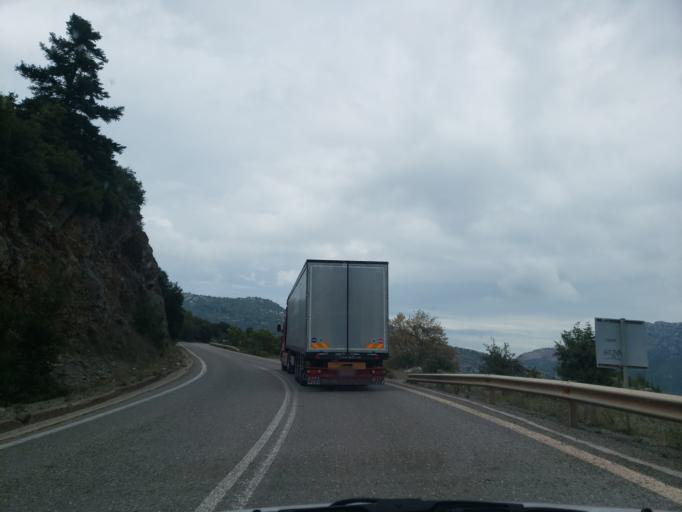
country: GR
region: Central Greece
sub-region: Nomos Fokidos
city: Amfissa
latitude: 38.6416
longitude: 22.3963
